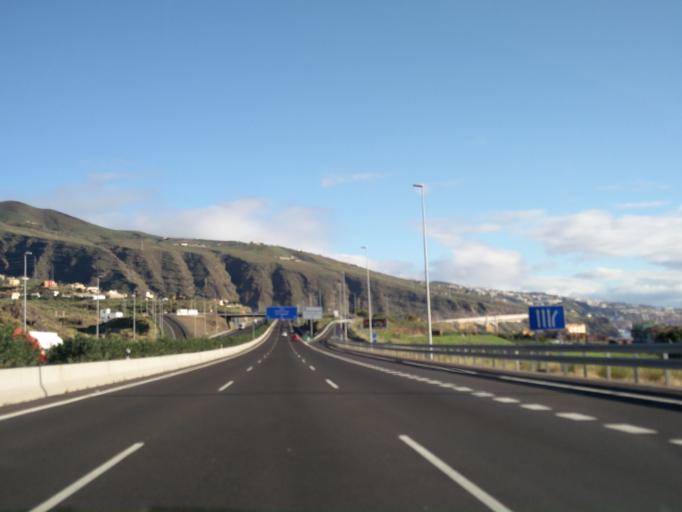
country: ES
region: Canary Islands
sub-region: Provincia de Santa Cruz de Tenerife
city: Candelaria
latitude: 28.3673
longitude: -16.3689
